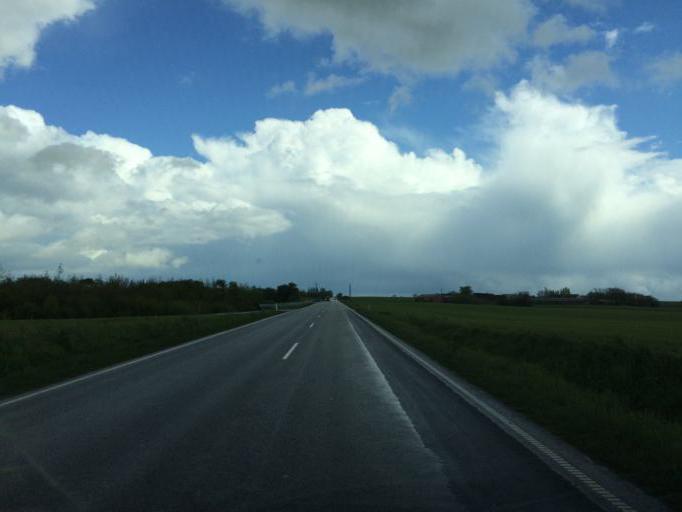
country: DK
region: Central Jutland
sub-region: Holstebro Kommune
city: Holstebro
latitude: 56.3857
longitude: 8.6531
